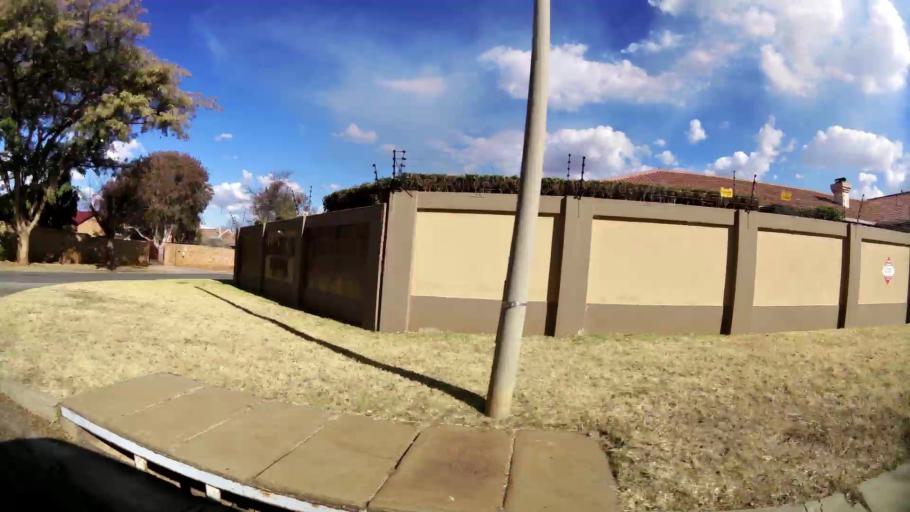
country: ZA
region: North-West
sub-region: Dr Kenneth Kaunda District Municipality
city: Klerksdorp
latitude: -26.8319
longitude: 26.6800
